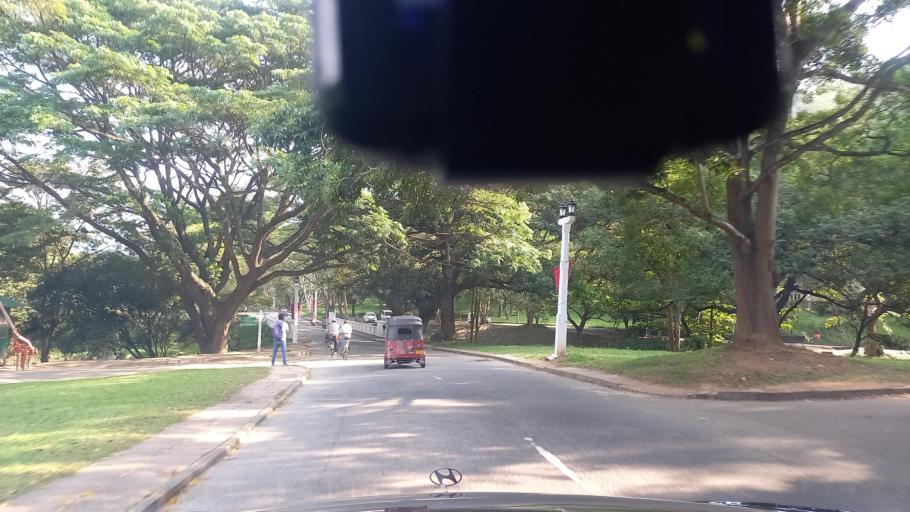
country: LK
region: Central
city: Kandy
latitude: 7.2556
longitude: 80.5991
